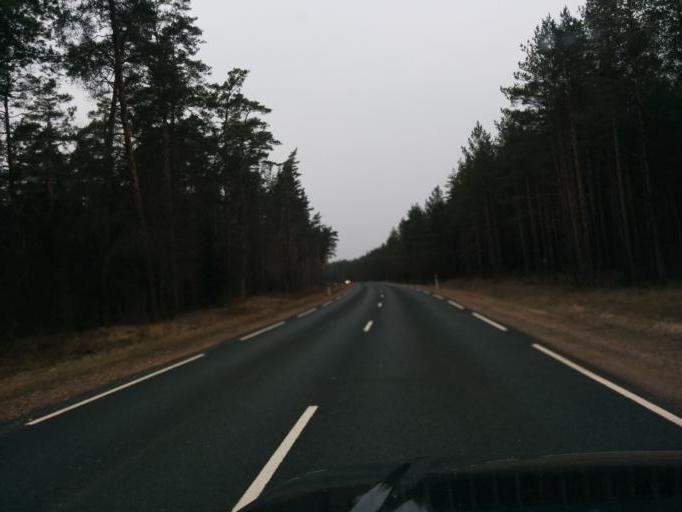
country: LV
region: Ogre
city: Ogre
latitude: 56.7990
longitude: 24.5902
